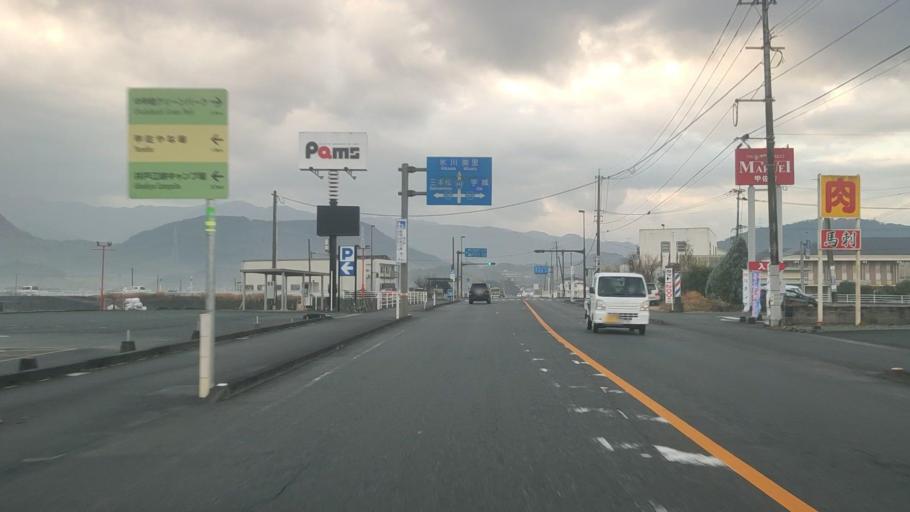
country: JP
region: Kumamoto
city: Matsubase
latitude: 32.6489
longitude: 130.8112
